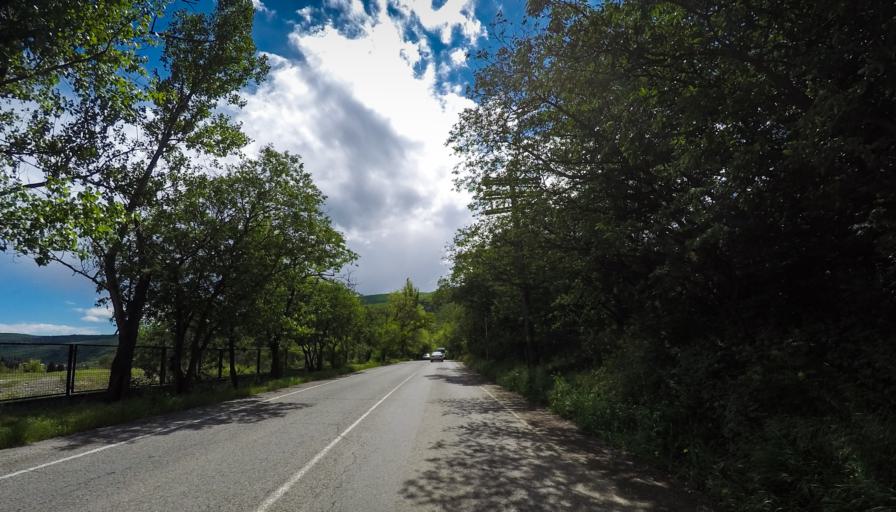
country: GE
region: Mtskheta-Mtianeti
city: Mtskheta
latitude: 41.8361
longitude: 44.7228
